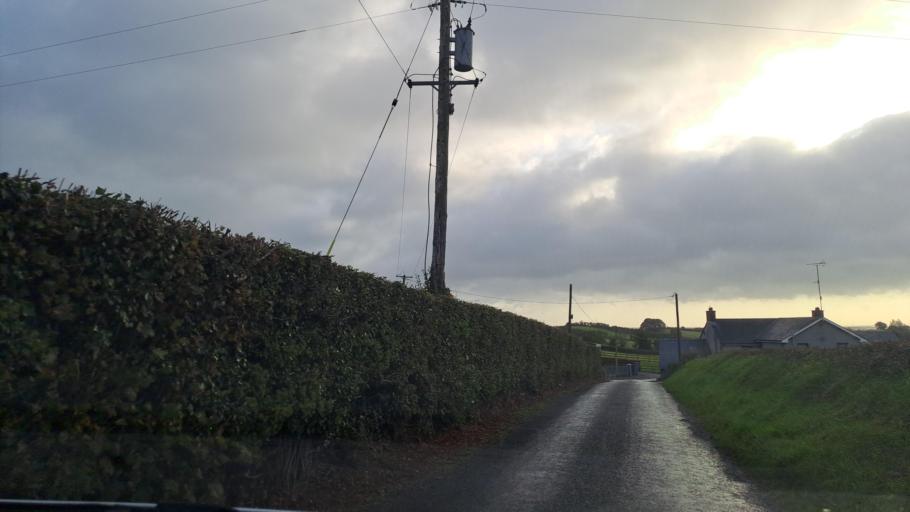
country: IE
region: Ulster
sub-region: An Cabhan
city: Kingscourt
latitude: 53.9597
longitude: -6.8139
